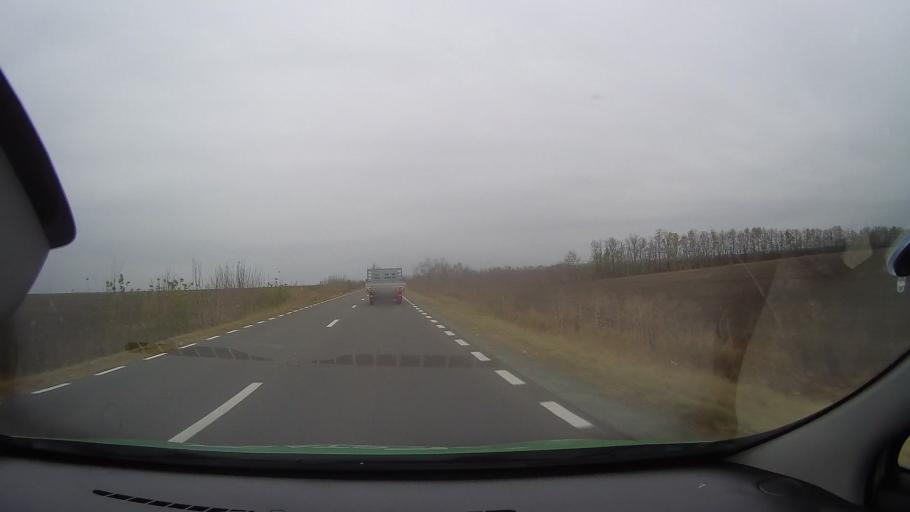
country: RO
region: Ialomita
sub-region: Comuna Scanteia
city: Iazu
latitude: 44.6789
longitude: 27.4186
